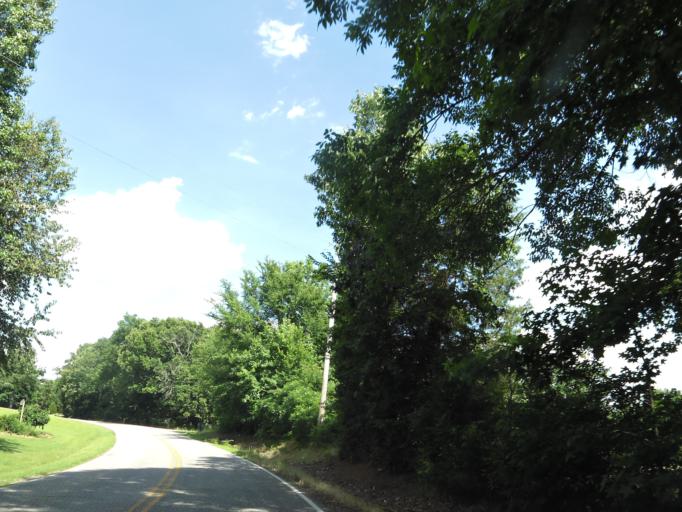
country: US
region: Tennessee
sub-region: Gibson County
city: Trenton
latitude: 35.9780
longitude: -88.8478
